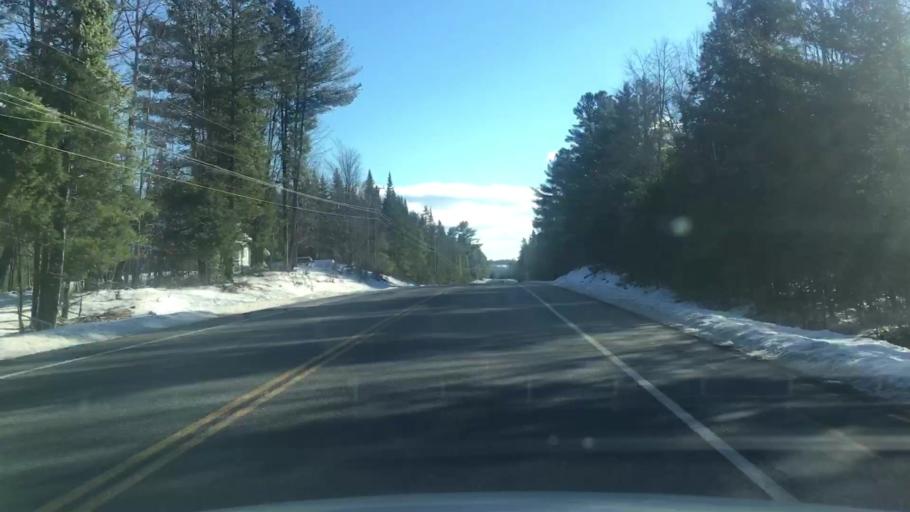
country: US
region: Maine
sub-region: Somerset County
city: Madison
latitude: 44.9203
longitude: -69.8256
